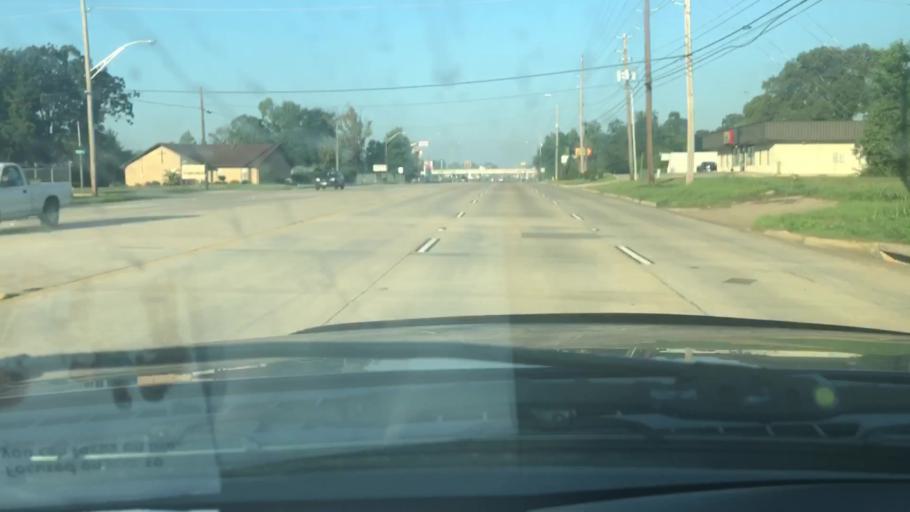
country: US
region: Texas
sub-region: Bowie County
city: Wake Village
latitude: 33.4195
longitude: -94.0908
